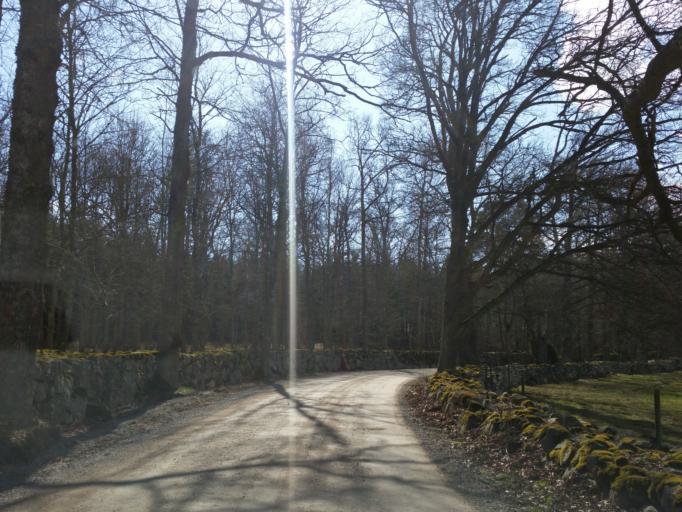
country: SE
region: Kalmar
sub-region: Monsteras Kommun
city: Timmernabben
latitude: 56.9440
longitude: 16.4267
